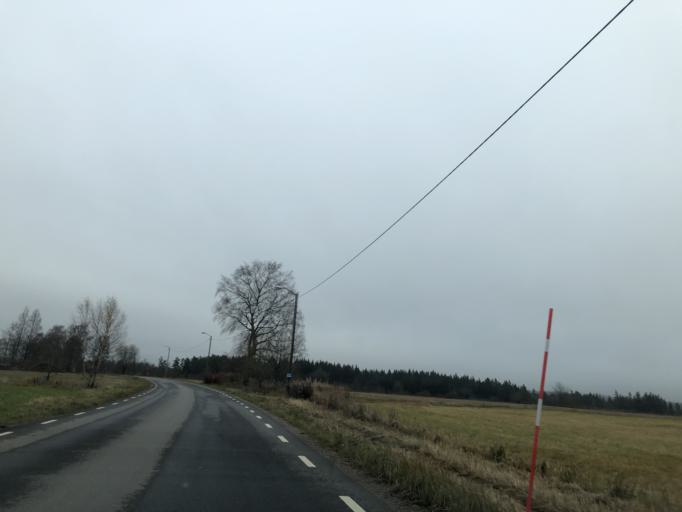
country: SE
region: Vaestra Goetaland
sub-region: Ulricehamns Kommun
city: Ulricehamn
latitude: 57.6815
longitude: 13.4723
